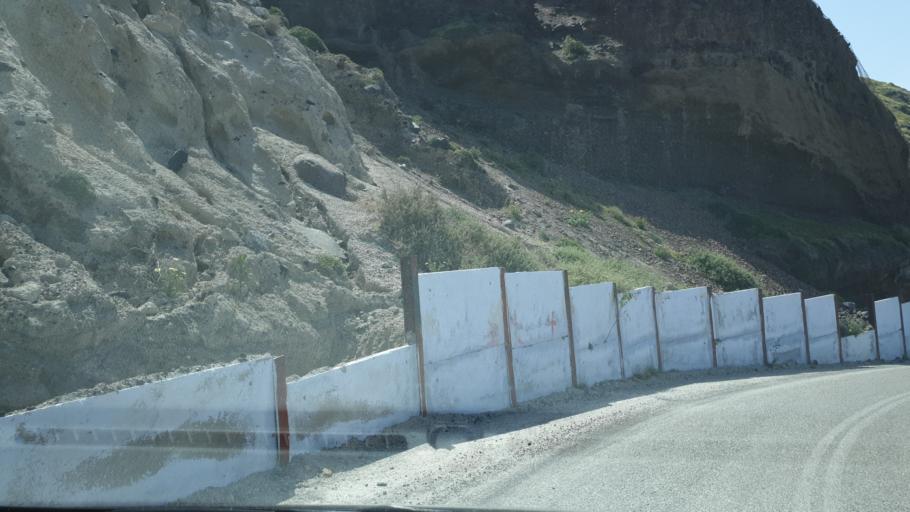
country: GR
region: South Aegean
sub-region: Nomos Kykladon
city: Oia
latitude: 36.4638
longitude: 25.3702
